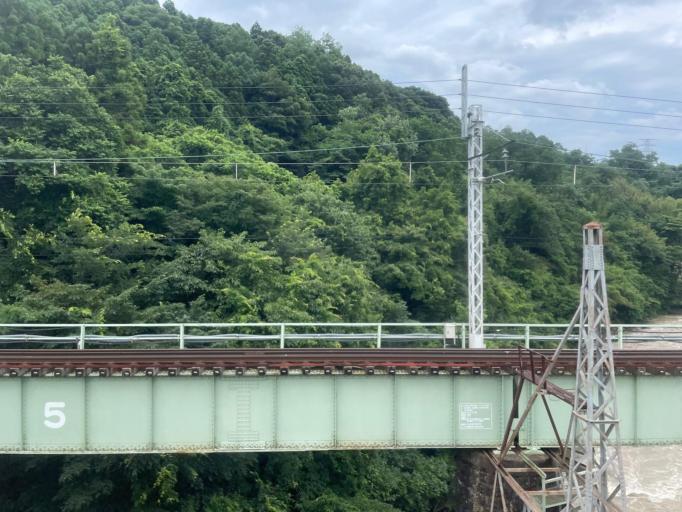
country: JP
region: Gunma
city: Numata
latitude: 36.6309
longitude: 139.0387
